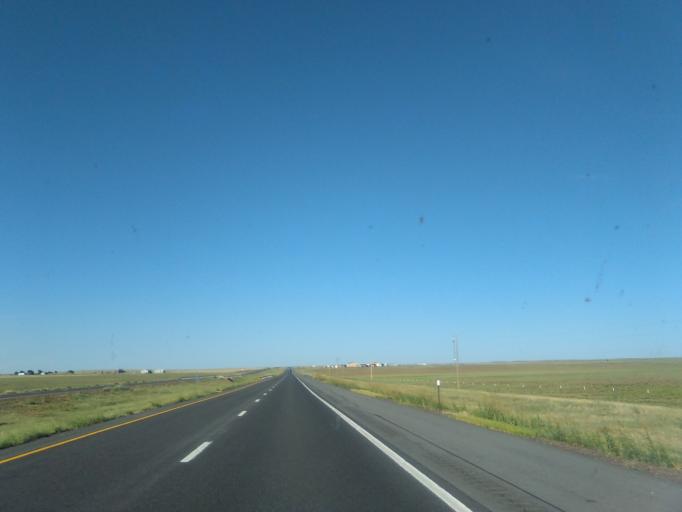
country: US
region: New Mexico
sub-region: San Miguel County
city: Las Vegas
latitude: 35.6892
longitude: -105.1348
